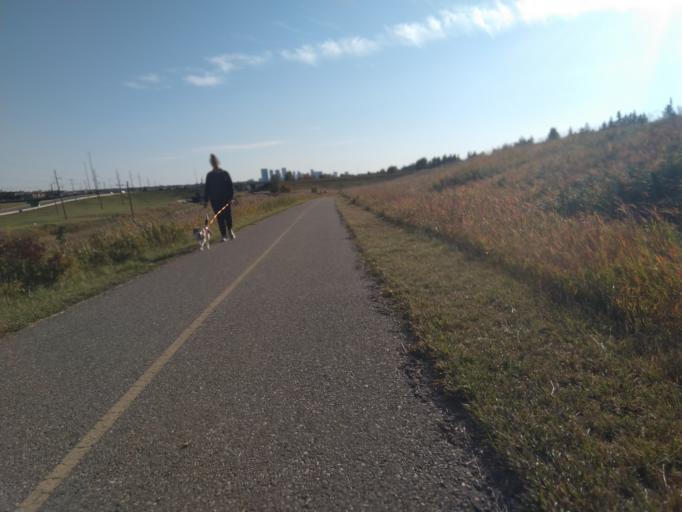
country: CA
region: Alberta
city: Calgary
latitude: 51.1152
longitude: -114.0490
